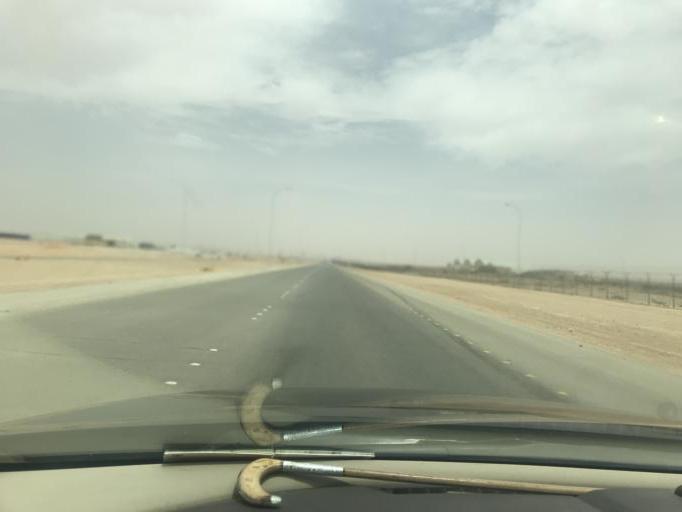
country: SA
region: Ar Riyad
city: Riyadh
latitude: 24.9535
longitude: 46.6741
